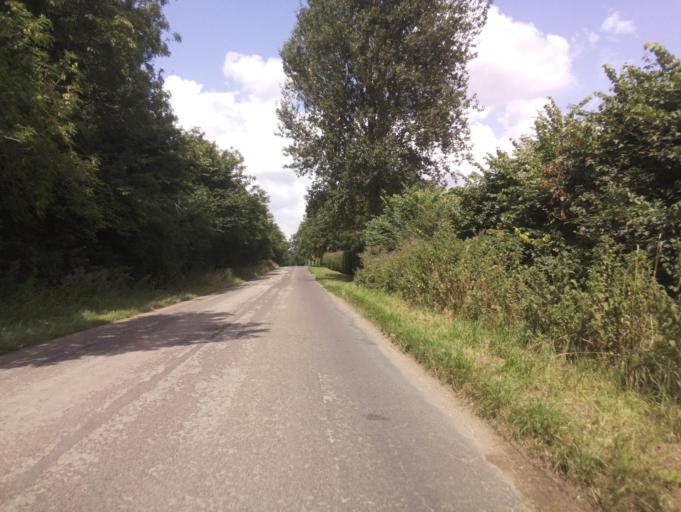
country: GB
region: England
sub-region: Wiltshire
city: Minety
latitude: 51.6087
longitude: -1.9545
